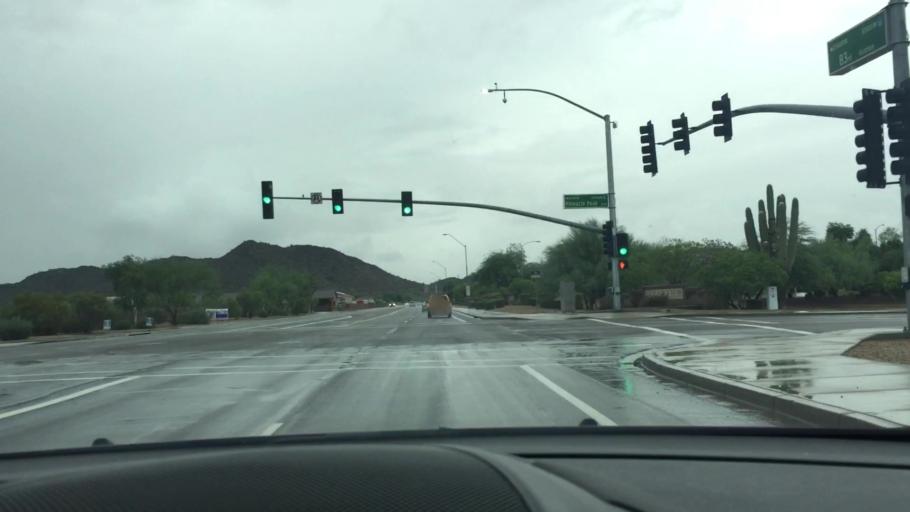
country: US
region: Arizona
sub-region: Maricopa County
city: Sun City
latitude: 33.6960
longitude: -112.2376
